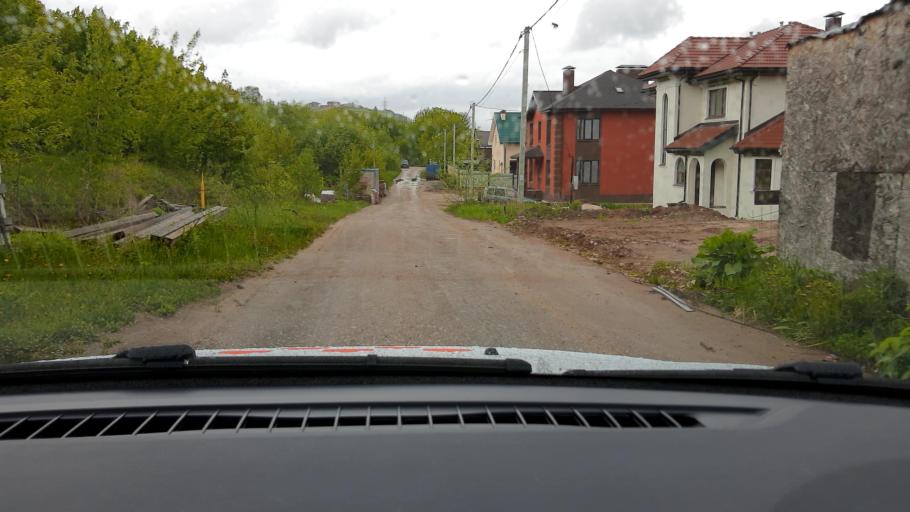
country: RU
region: Nizjnij Novgorod
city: Afonino
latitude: 56.2702
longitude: 44.0988
